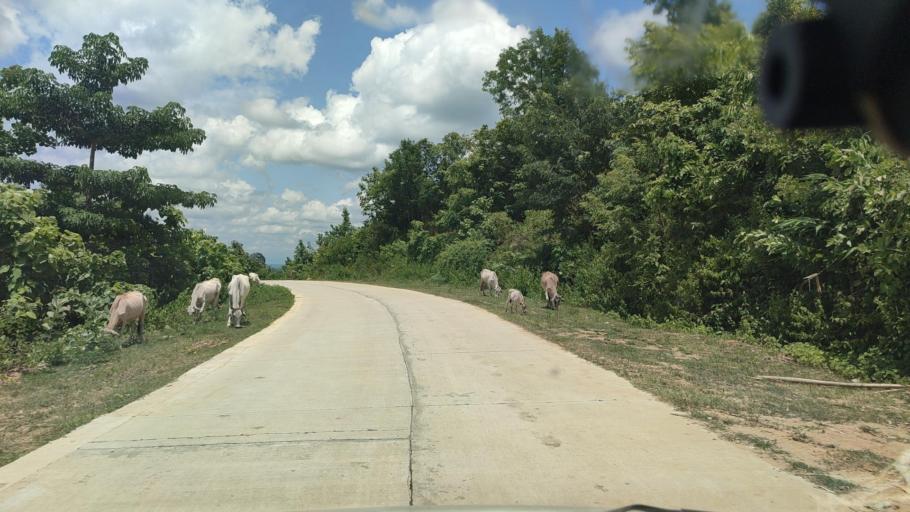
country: MM
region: Magway
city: Taungdwingyi
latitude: 20.0190
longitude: 95.8142
